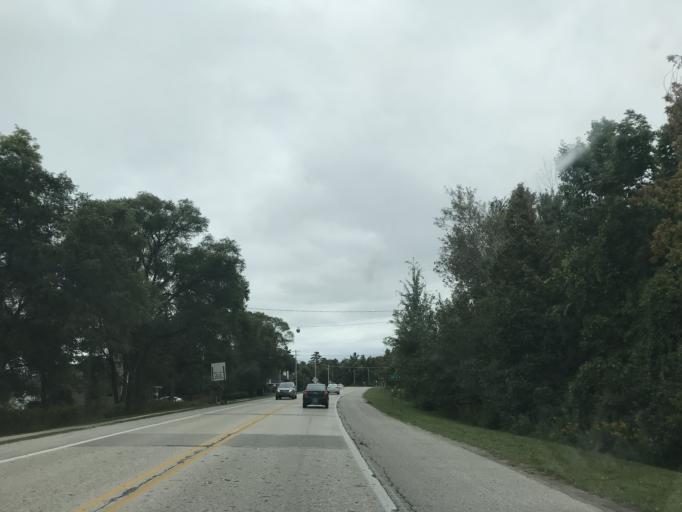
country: US
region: Michigan
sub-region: Leelanau County
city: Leland
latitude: 44.9730
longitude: -85.6502
